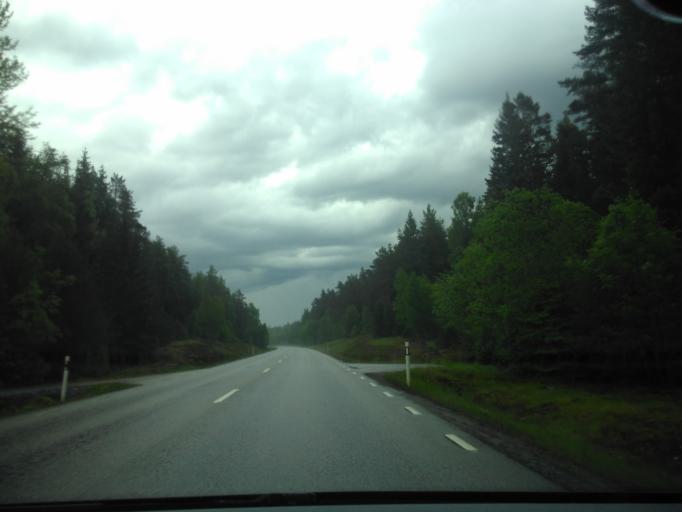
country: SE
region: Vaestra Goetaland
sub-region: Herrljunga Kommun
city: Herrljunga
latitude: 58.0582
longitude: 13.0589
